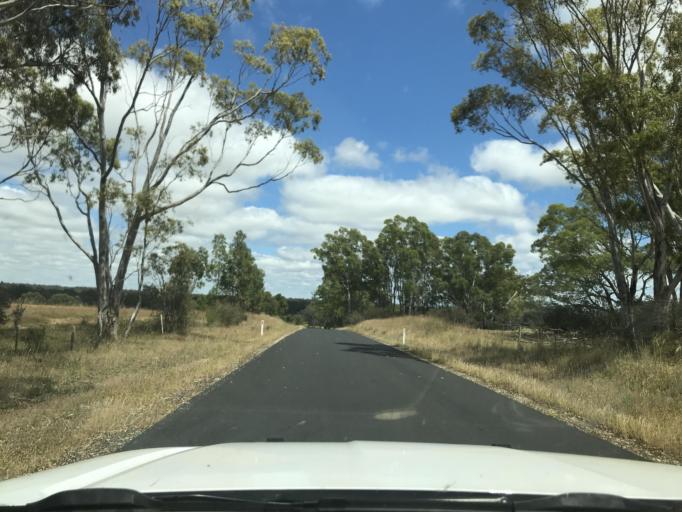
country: AU
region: South Australia
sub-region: Naracoorte and Lucindale
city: Naracoorte
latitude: -36.6822
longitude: 141.3014
